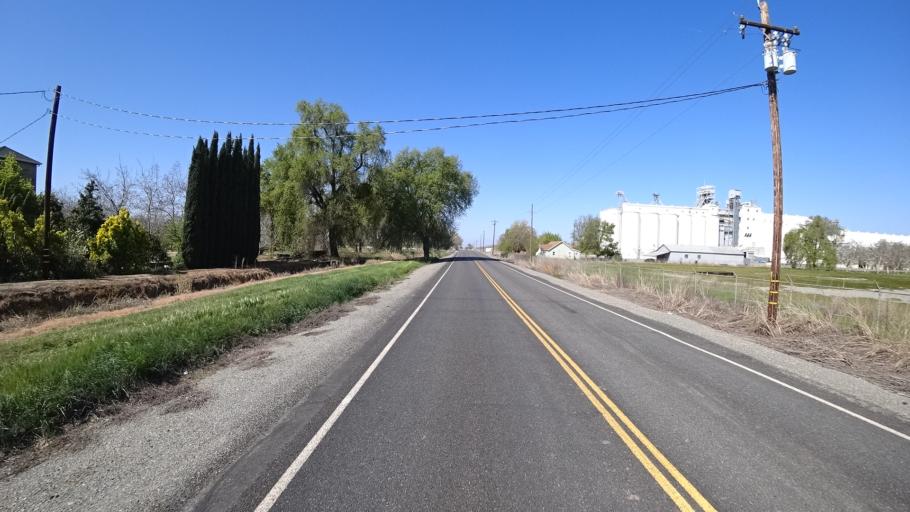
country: US
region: California
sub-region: Glenn County
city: Willows
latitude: 39.4574
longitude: -122.0199
